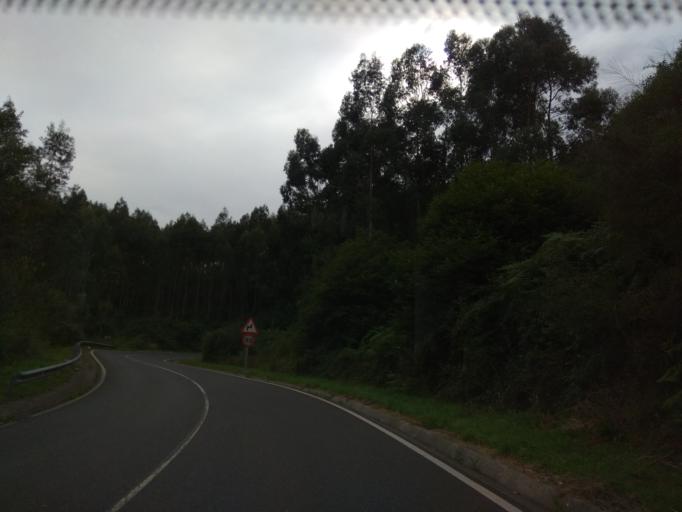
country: ES
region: Cantabria
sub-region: Provincia de Cantabria
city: Hazas de Cesto
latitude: 43.4044
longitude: -3.5995
